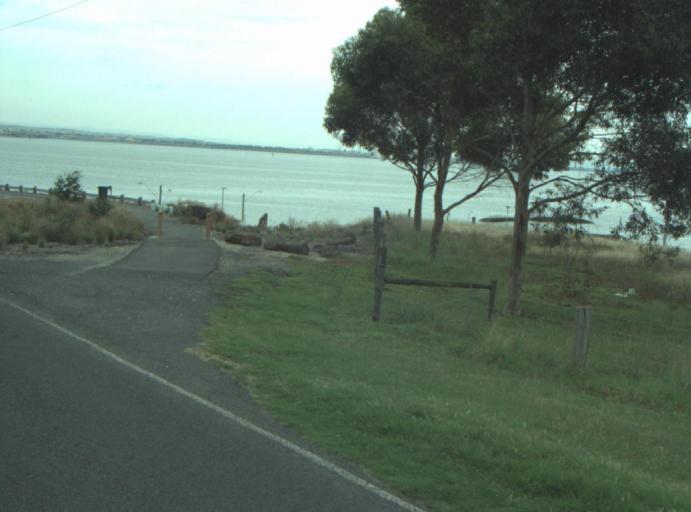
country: AU
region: Victoria
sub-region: Greater Geelong
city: East Geelong
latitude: -38.1455
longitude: 144.3848
